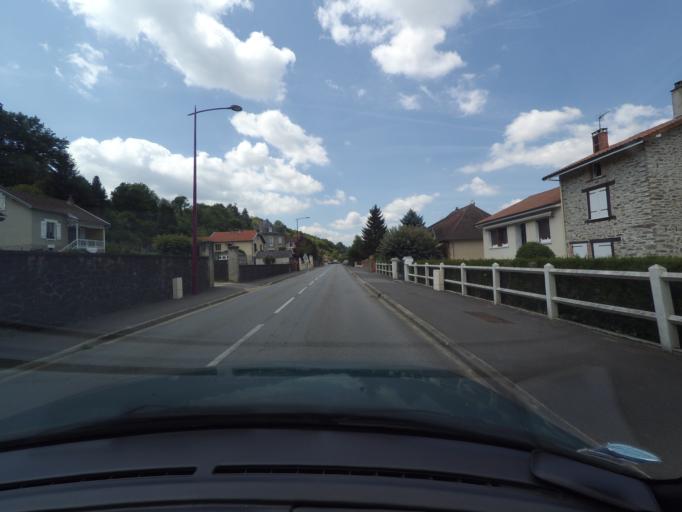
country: FR
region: Limousin
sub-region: Departement de la Haute-Vienne
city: Isle
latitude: 45.7797
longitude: 1.1978
